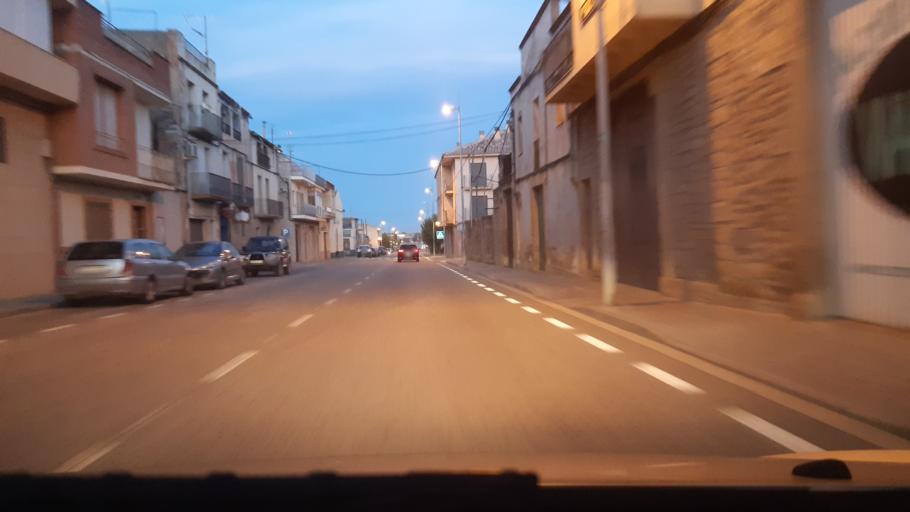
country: ES
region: Aragon
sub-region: Provincia de Teruel
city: Calaceite
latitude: 41.0159
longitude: 0.1903
